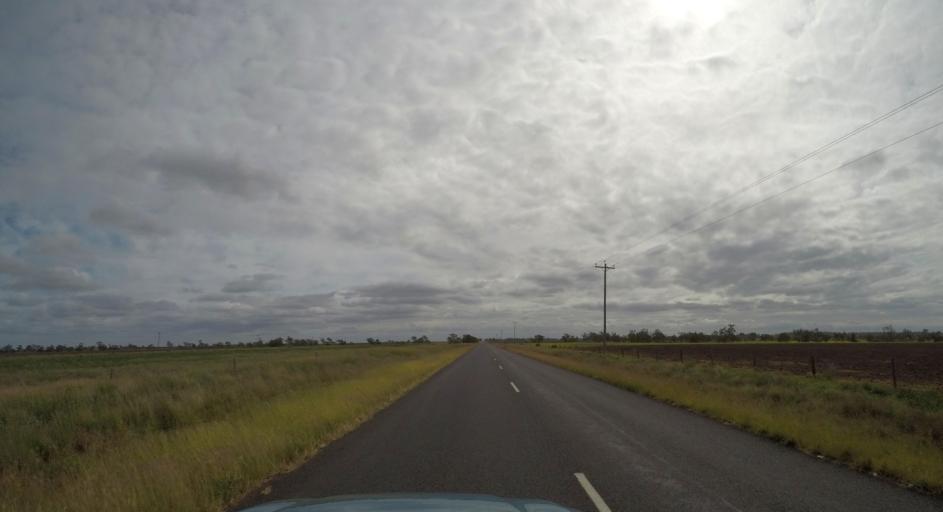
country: AU
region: Queensland
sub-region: Western Downs
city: Dalby
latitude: -26.9880
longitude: 151.2275
